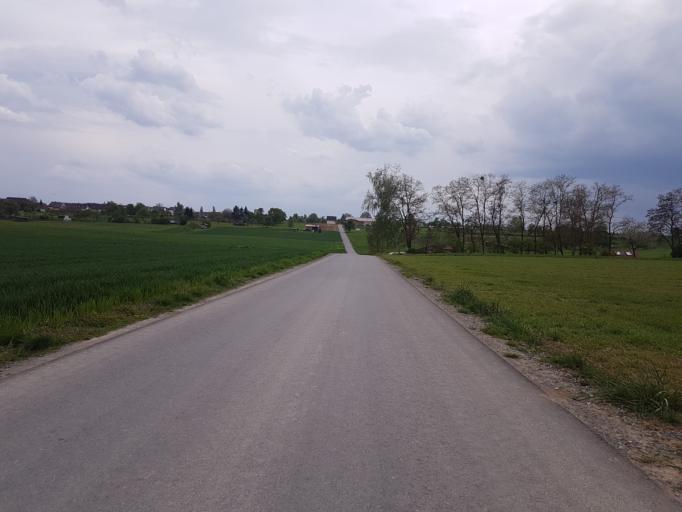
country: DE
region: Baden-Wuerttemberg
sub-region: Regierungsbezirk Stuttgart
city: Bondorf
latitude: 48.5280
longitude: 8.8220
